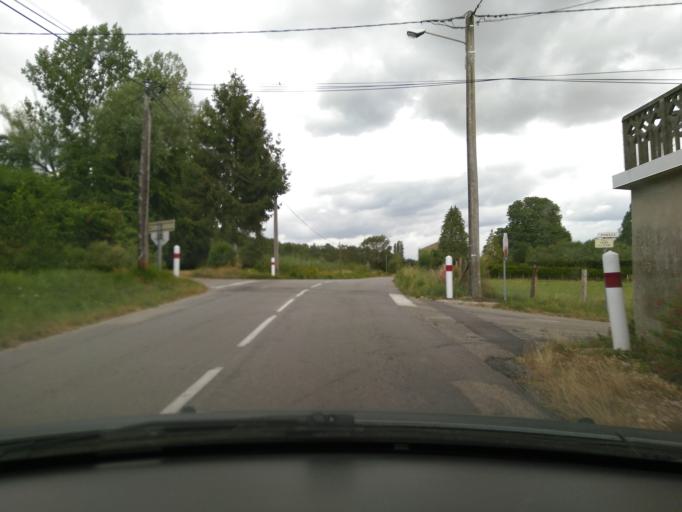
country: FR
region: Rhone-Alpes
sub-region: Departement de l'Isere
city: Chatonnay
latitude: 45.4189
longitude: 5.1584
